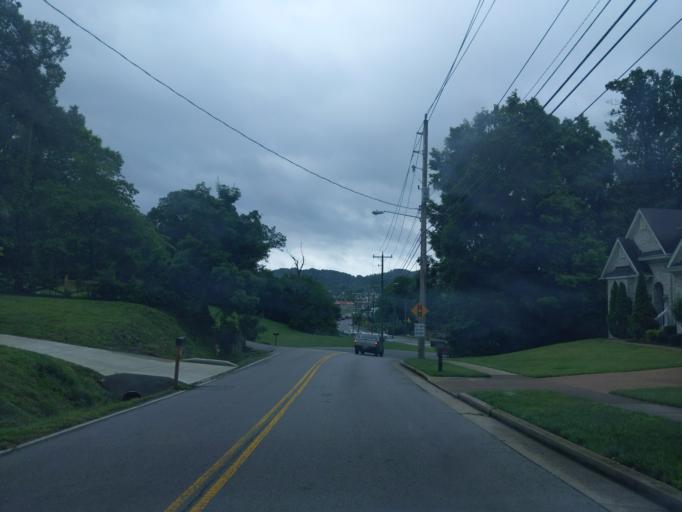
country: US
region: Tennessee
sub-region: Williamson County
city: Brentwood Estates
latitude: 36.0423
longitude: -86.7502
